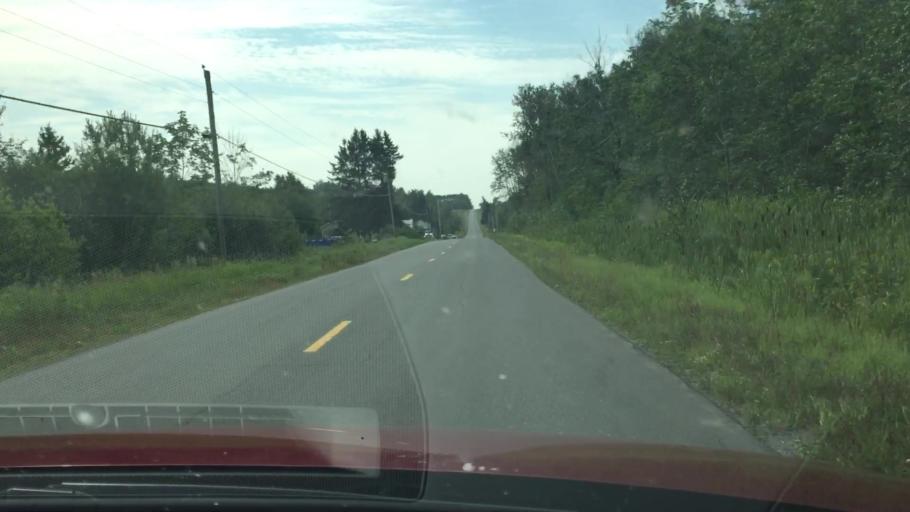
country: US
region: Maine
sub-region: Aroostook County
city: Caribou
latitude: 46.8130
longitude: -68.0245
